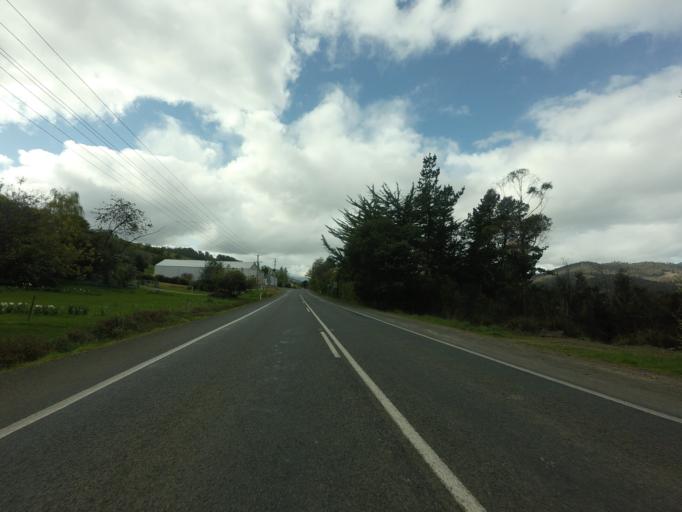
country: AU
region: Tasmania
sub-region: Huon Valley
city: Franklin
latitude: -43.0982
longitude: 147.0055
